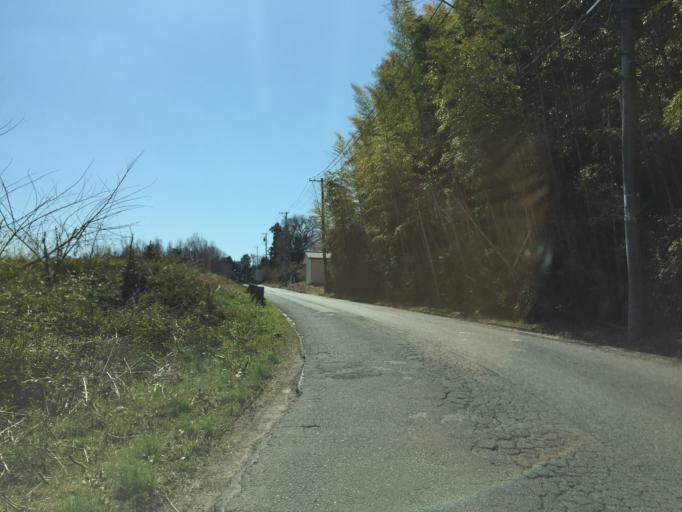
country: JP
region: Fukushima
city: Iwaki
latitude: 37.0563
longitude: 140.8399
